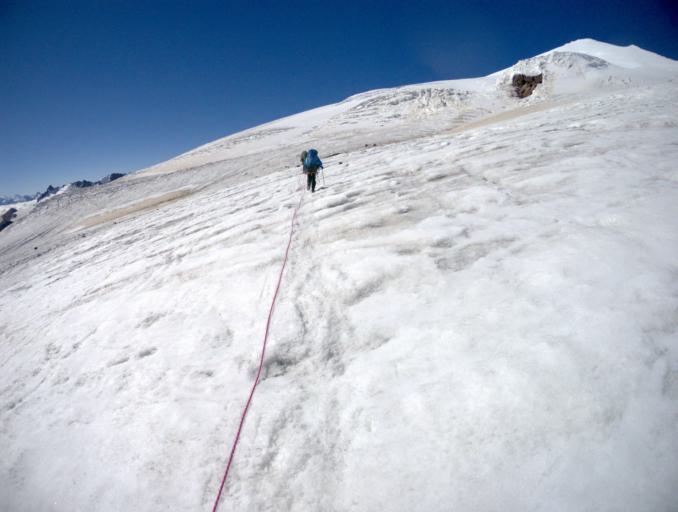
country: RU
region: Kabardino-Balkariya
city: Terskol
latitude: 43.3690
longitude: 42.4955
